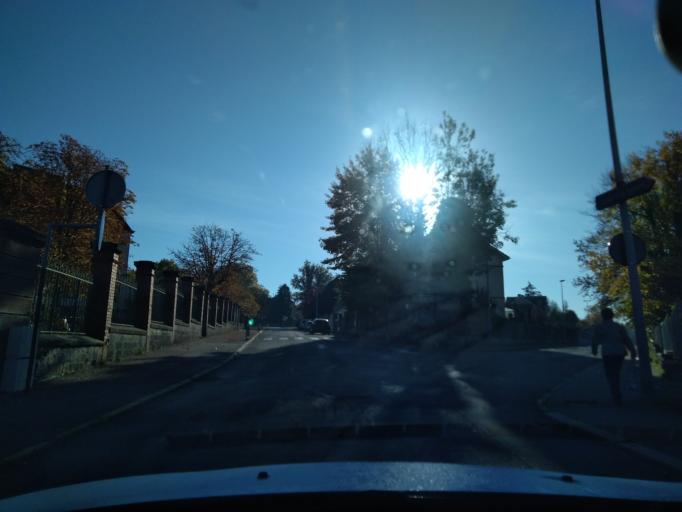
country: FR
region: Lorraine
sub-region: Departement de la Moselle
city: Sarreguemines
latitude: 49.1117
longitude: 7.0729
